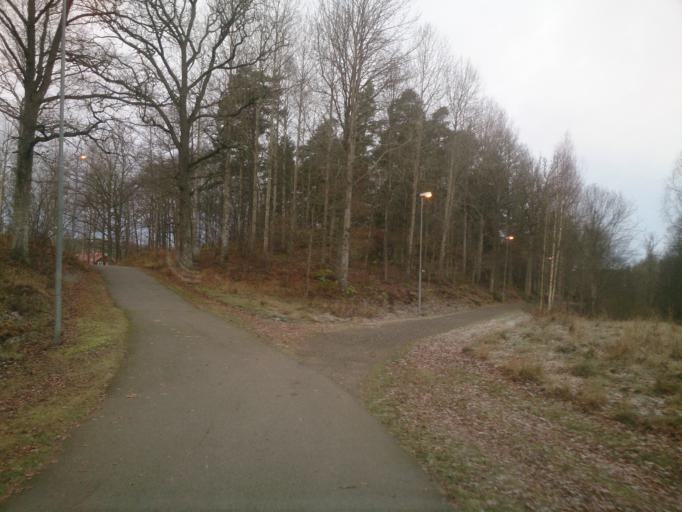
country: SE
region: OEstergoetland
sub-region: Atvidabergs Kommun
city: Atvidaberg
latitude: 58.2034
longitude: 15.9770
